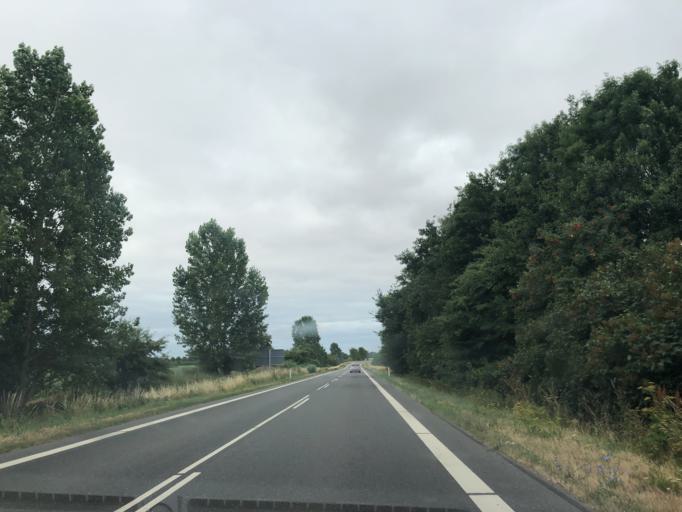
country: DK
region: Zealand
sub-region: Slagelse Kommune
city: Skaelskor
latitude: 55.2536
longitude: 11.3249
